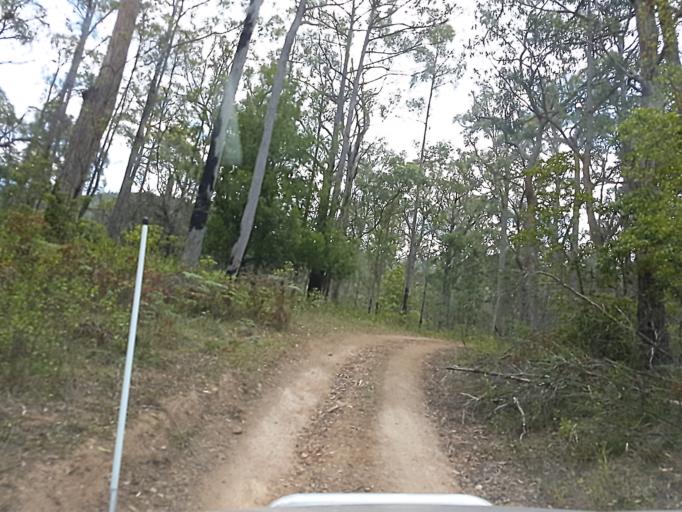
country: AU
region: Victoria
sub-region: East Gippsland
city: Lakes Entrance
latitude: -37.3521
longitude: 148.3559
